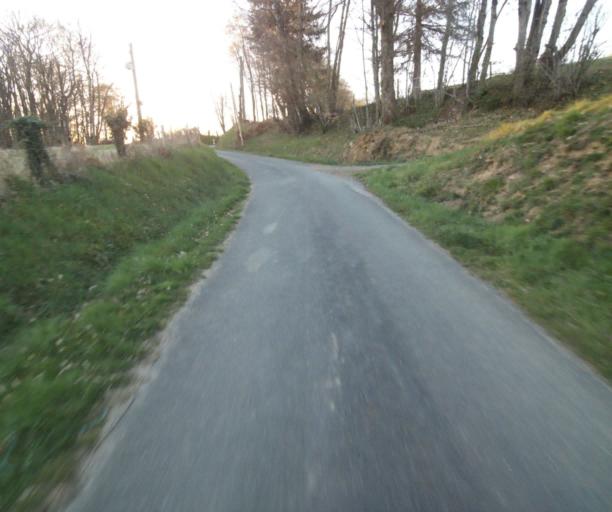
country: FR
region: Limousin
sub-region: Departement de la Correze
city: Uzerche
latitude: 45.3726
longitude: 1.6099
